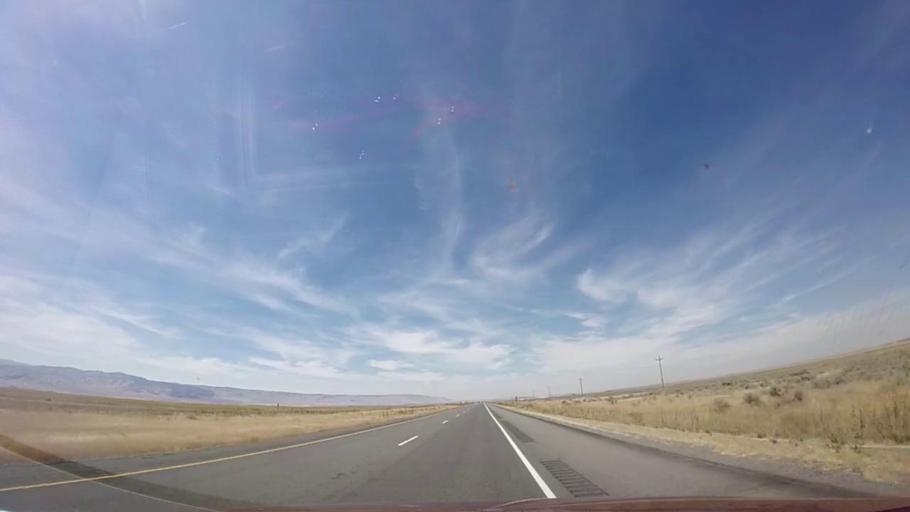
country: US
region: Idaho
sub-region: Minidoka County
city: Rupert
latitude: 42.3562
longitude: -113.2498
